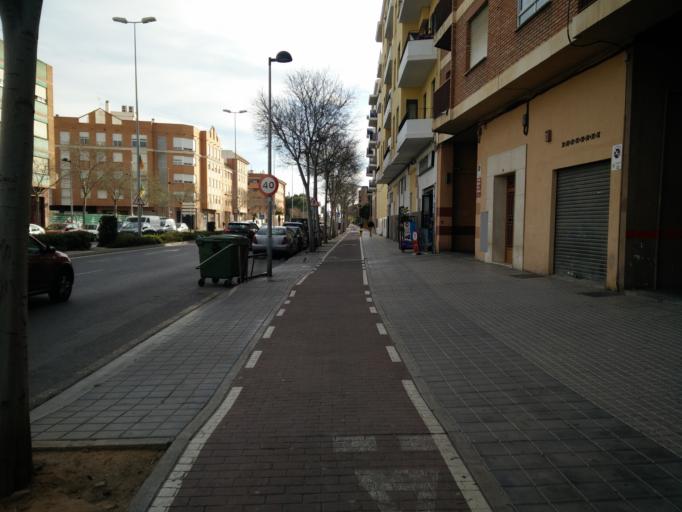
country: ES
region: Valencia
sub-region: Provincia de Castello
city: Castello de la Plana
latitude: 39.9853
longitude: -0.0497
